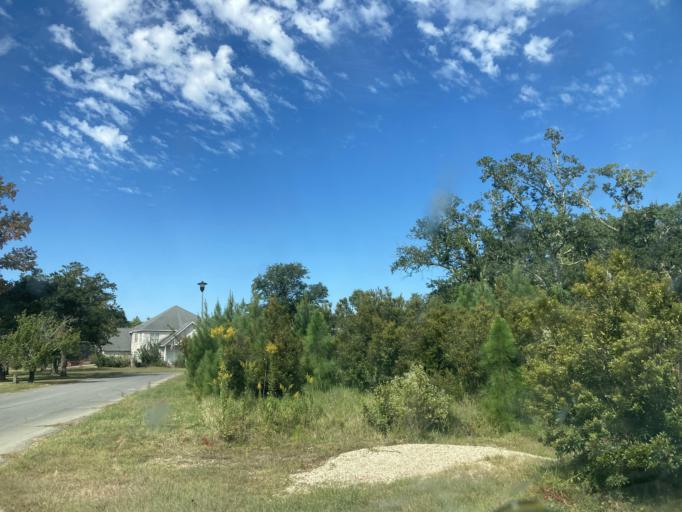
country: US
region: Mississippi
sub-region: Jackson County
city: Gulf Hills
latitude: 30.4367
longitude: -88.8520
